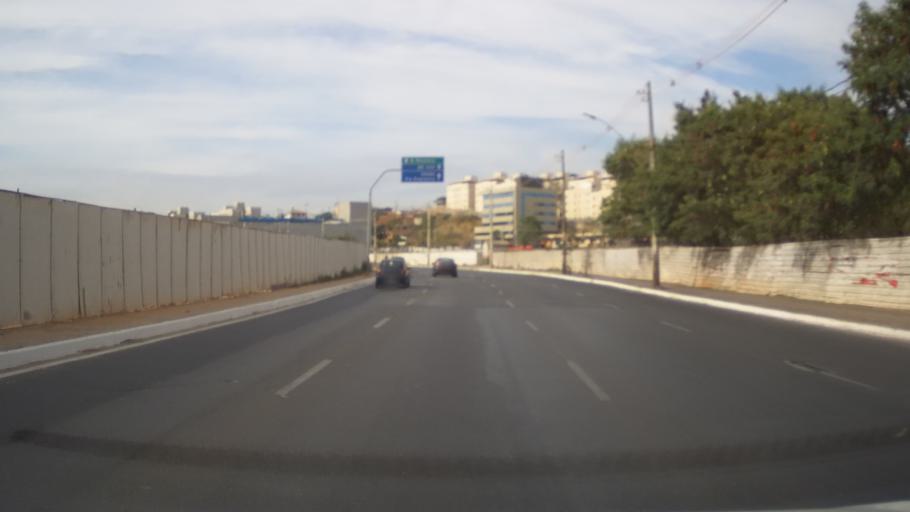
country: BR
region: Minas Gerais
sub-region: Contagem
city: Contagem
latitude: -19.8827
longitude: -44.0388
